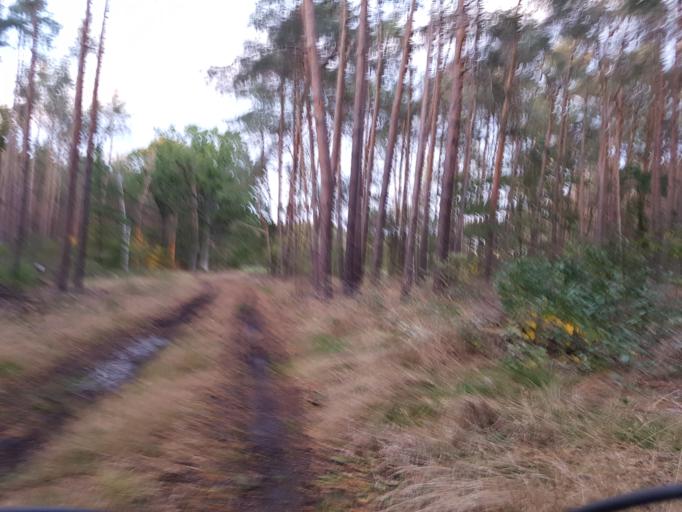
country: DE
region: Brandenburg
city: Schilda
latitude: 51.6001
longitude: 13.3658
